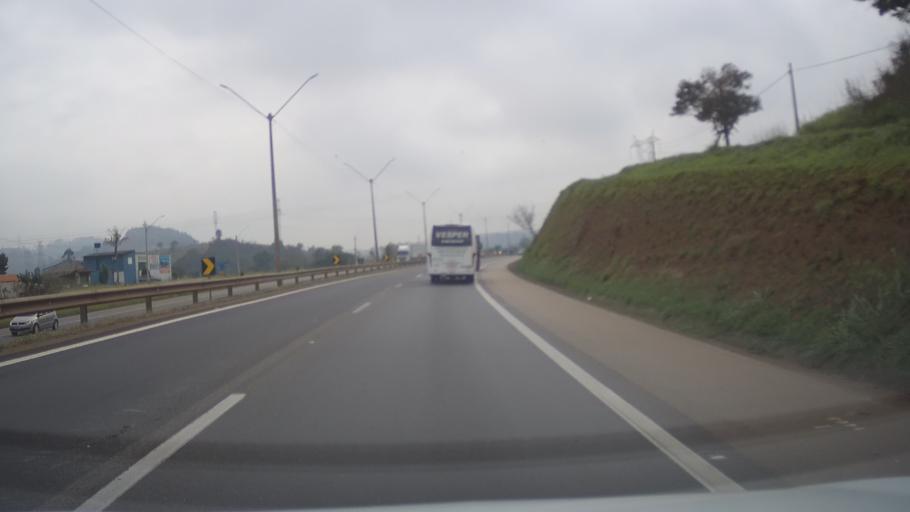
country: BR
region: Sao Paulo
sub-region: Atibaia
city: Atibaia
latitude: -23.0372
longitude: -46.5540
